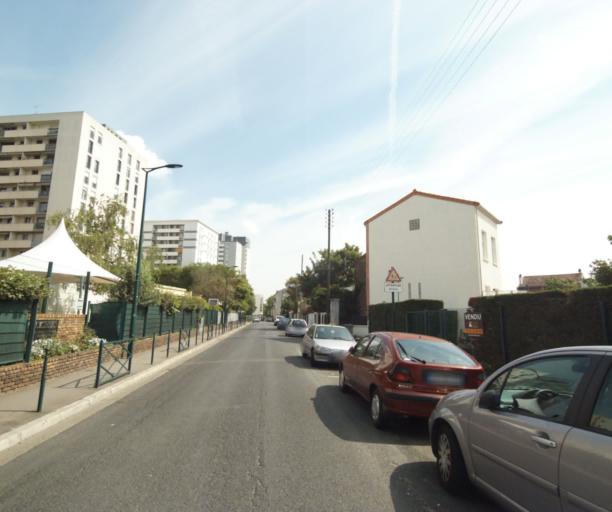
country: FR
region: Ile-de-France
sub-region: Departement des Hauts-de-Seine
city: Colombes
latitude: 48.9202
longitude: 2.2468
